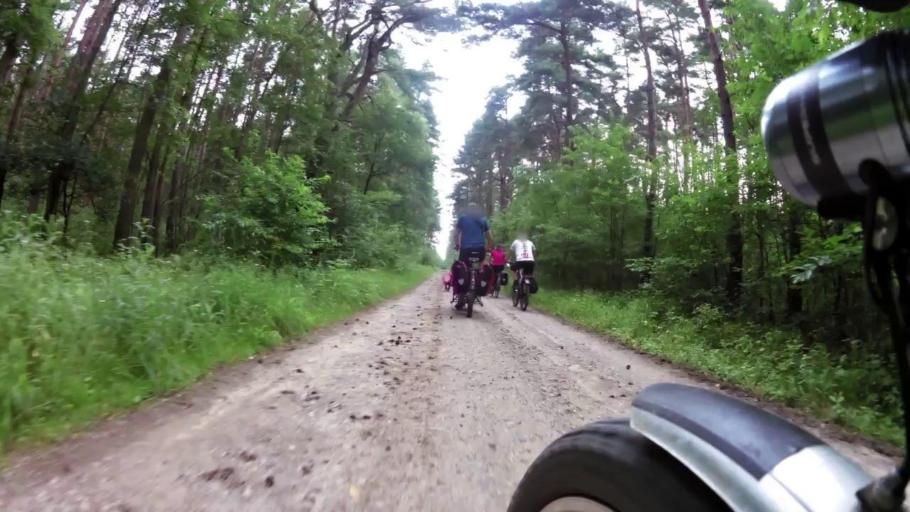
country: PL
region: West Pomeranian Voivodeship
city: Trzcinsko Zdroj
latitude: 52.8584
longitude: 14.6041
